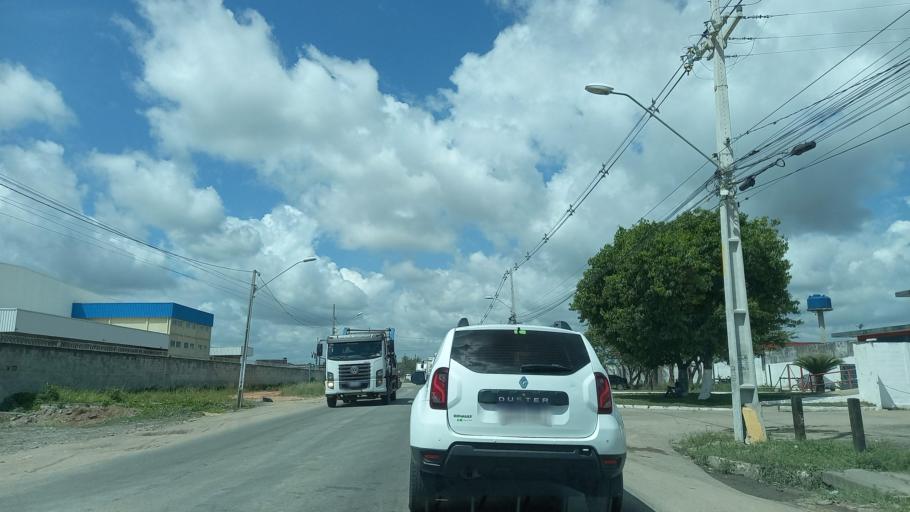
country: BR
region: Pernambuco
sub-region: Jaboatao Dos Guararapes
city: Jaboatao
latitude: -8.1559
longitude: -34.9655
